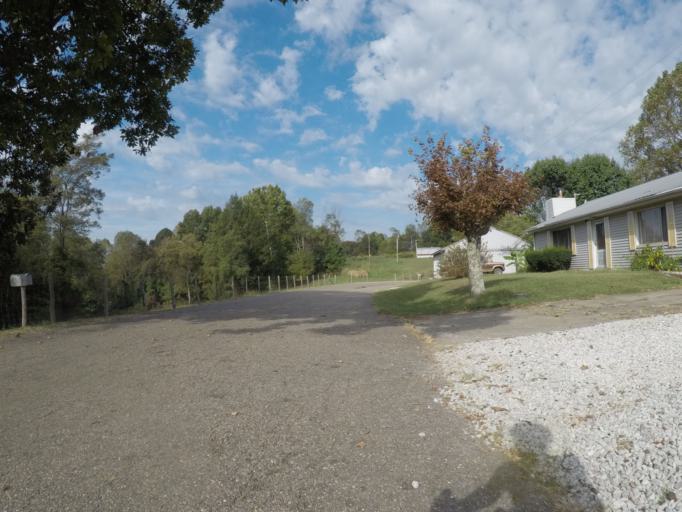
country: US
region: West Virginia
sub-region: Cabell County
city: Lesage
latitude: 38.5690
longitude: -82.4289
